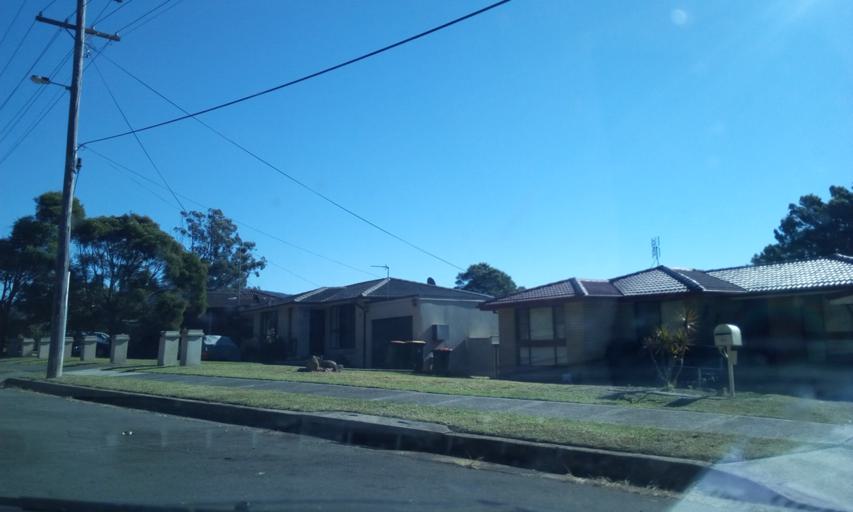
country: AU
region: New South Wales
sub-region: Wollongong
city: Dapto
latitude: -34.5168
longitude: 150.7811
